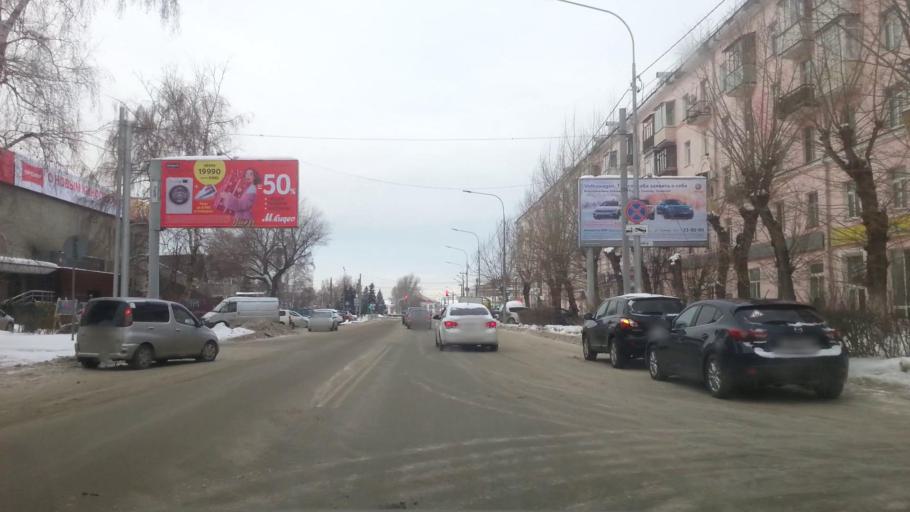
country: RU
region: Altai Krai
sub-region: Gorod Barnaulskiy
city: Barnaul
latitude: 53.3493
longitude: 83.7645
